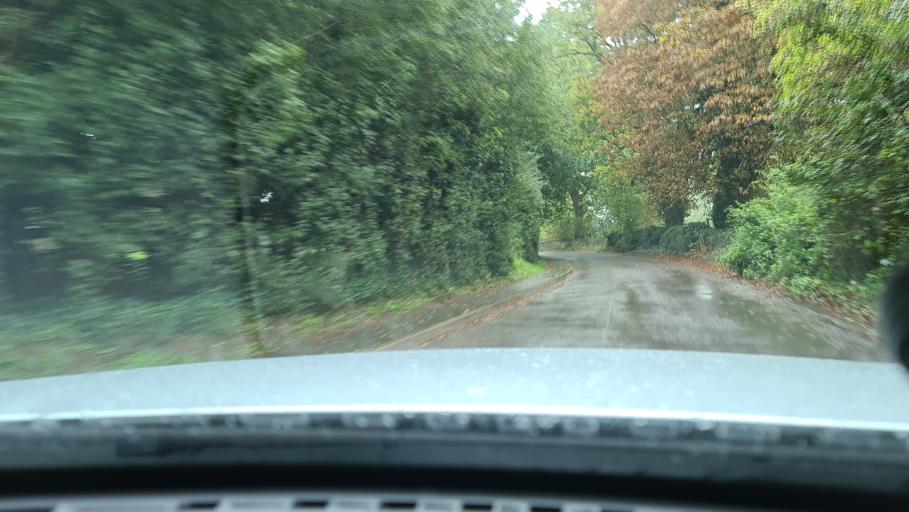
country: GB
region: England
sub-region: Oxfordshire
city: Somerton
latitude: 51.9333
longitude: -1.3182
